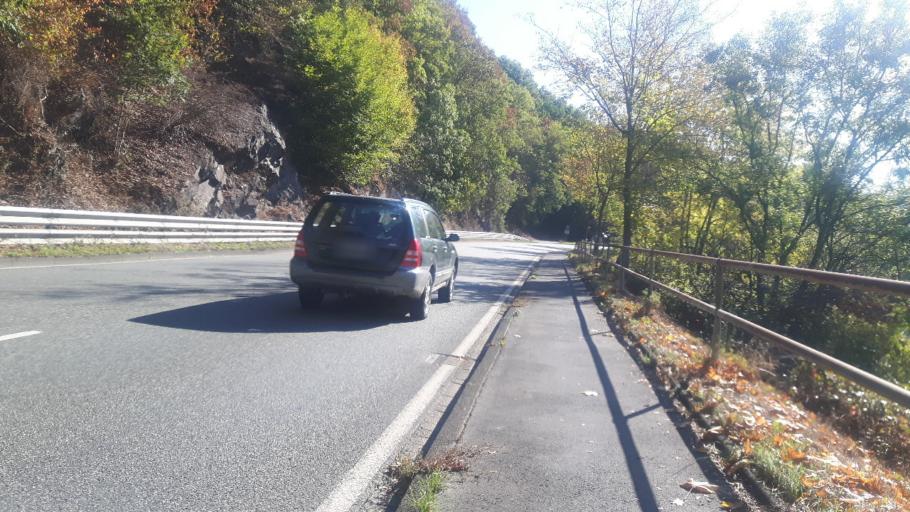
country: DE
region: Rheinland-Pfalz
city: Niederirsen
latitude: 50.8112
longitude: 7.6058
